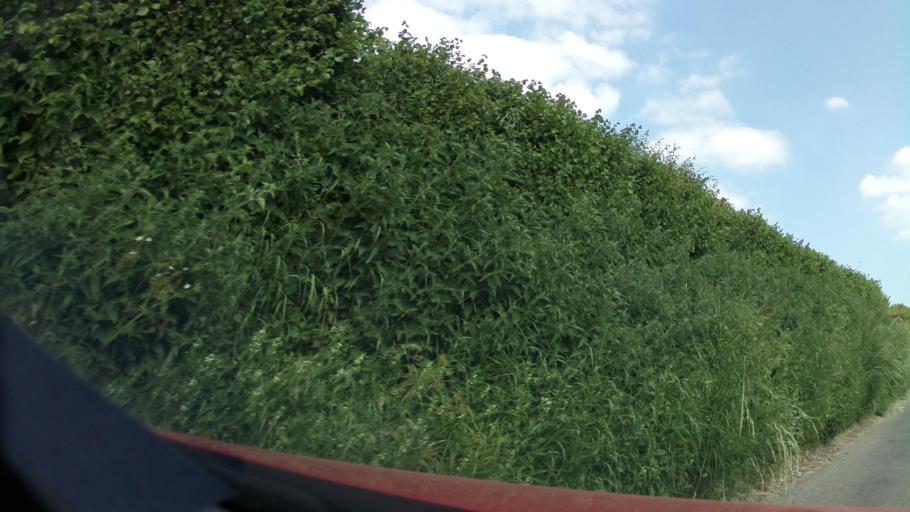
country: GB
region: England
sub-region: Wiltshire
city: Rushall
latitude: 51.2569
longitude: -1.7958
